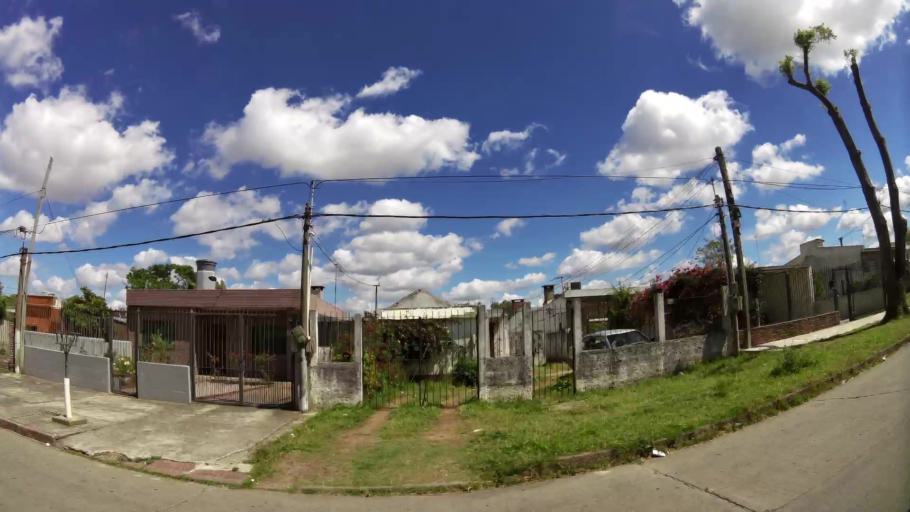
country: UY
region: Canelones
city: Paso de Carrasco
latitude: -34.8397
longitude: -56.1268
